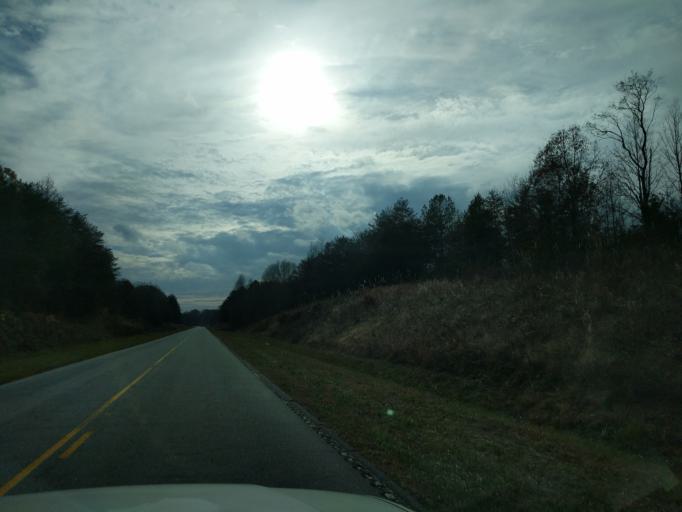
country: US
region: Georgia
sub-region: Franklin County
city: Gumlog
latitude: 34.5676
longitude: -83.0484
